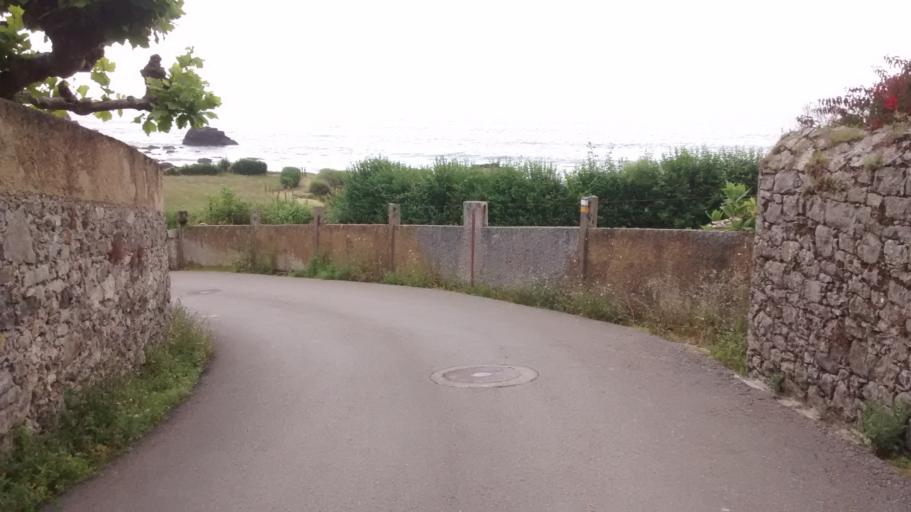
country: ES
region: Asturias
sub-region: Province of Asturias
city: Colunga
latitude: 43.4842
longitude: -5.2259
